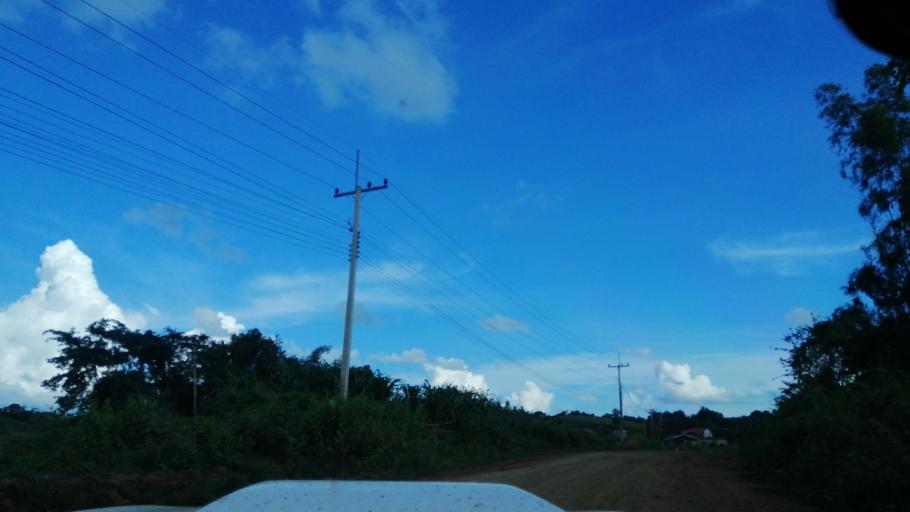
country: LA
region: Xiagnabouli
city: Muang Kenthao
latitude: 17.8484
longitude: 101.2438
